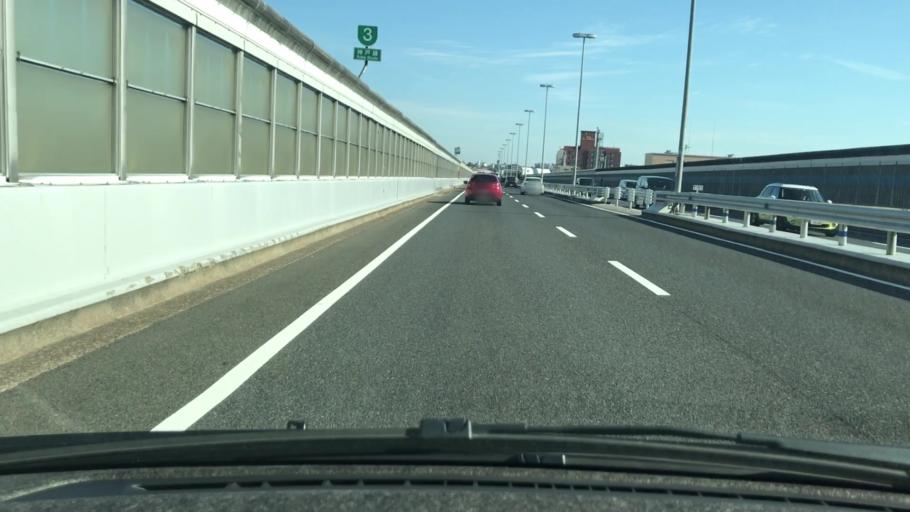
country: JP
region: Hyogo
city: Ashiya
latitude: 34.7290
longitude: 135.3128
